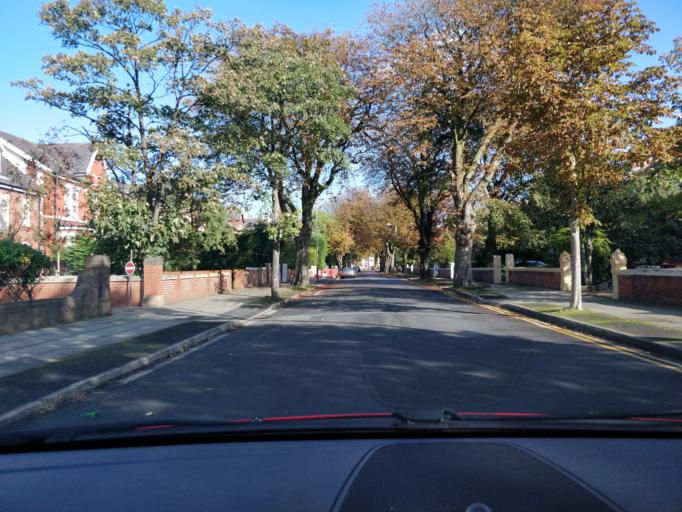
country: GB
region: England
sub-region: Sefton
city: Southport
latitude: 53.6394
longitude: -2.9847
